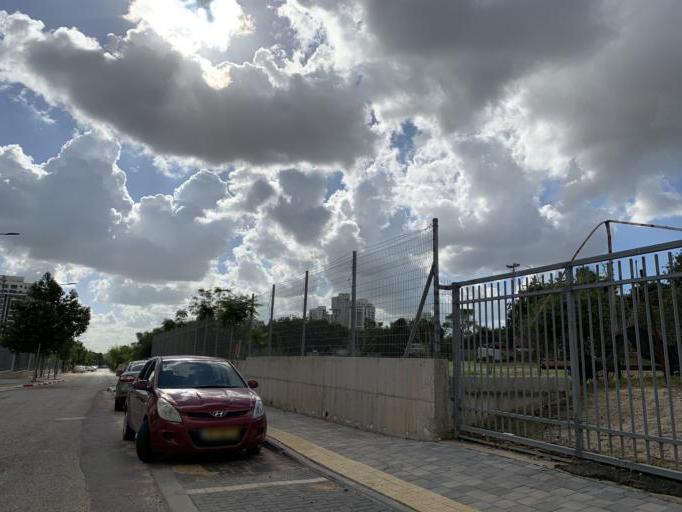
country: IL
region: Central District
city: Hod HaSharon
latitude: 32.1676
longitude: 34.8978
